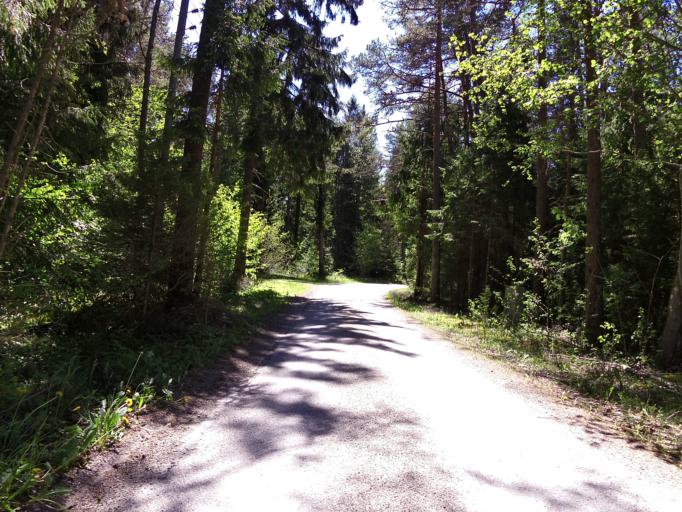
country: EE
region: Harju
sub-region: Paldiski linn
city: Paldiski
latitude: 59.2704
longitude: 23.7774
